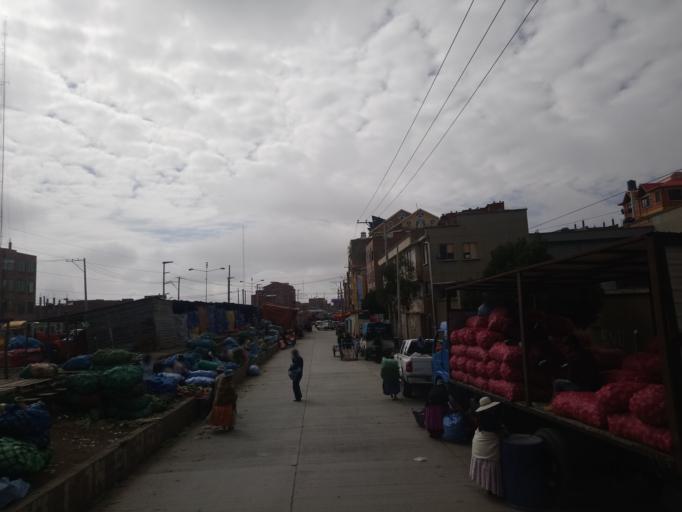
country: BO
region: La Paz
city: La Paz
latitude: -16.5091
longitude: -68.1556
